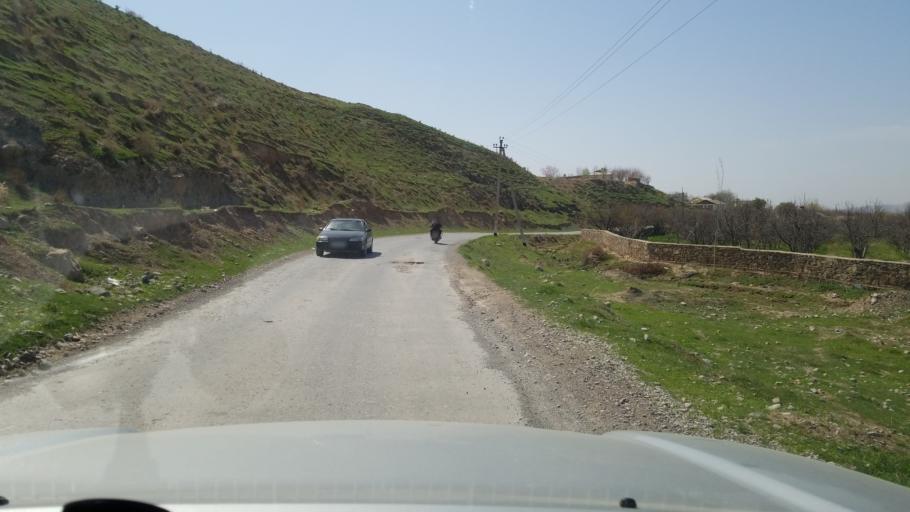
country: TM
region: Lebap
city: Gowurdak
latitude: 37.8836
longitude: 66.4599
